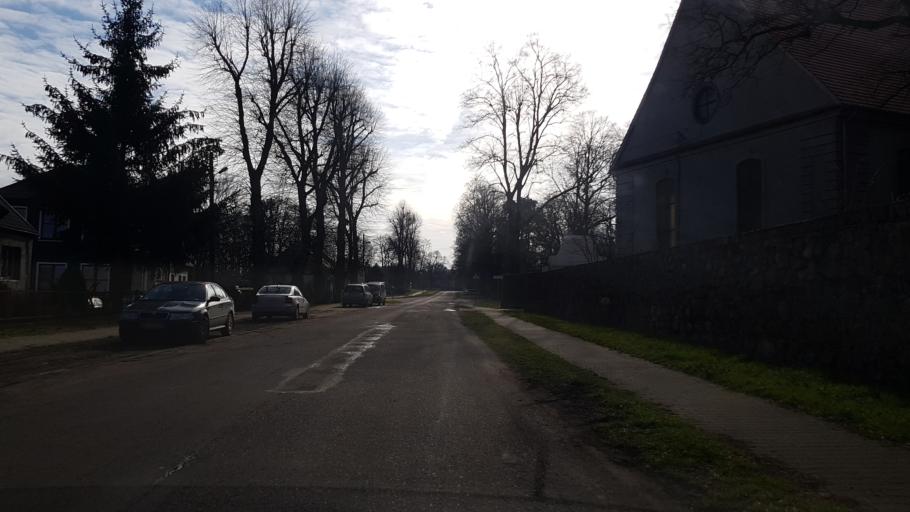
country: PL
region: West Pomeranian Voivodeship
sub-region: Powiat policki
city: Dobra
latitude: 53.5579
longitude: 14.3147
